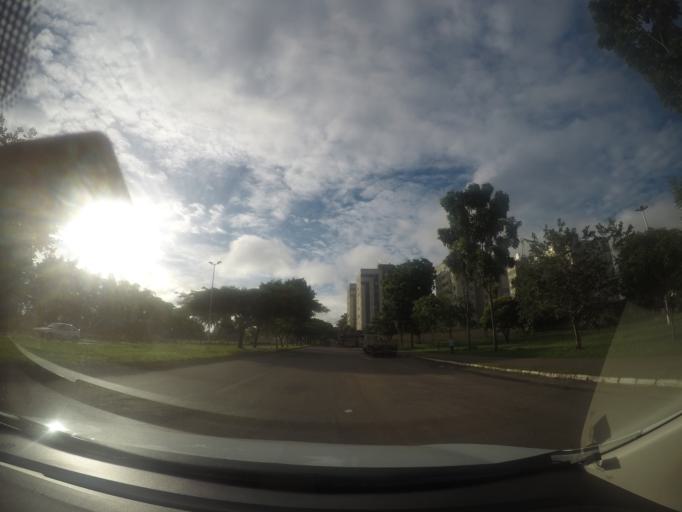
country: BR
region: Goias
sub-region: Goiania
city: Goiania
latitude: -16.6875
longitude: -49.3076
